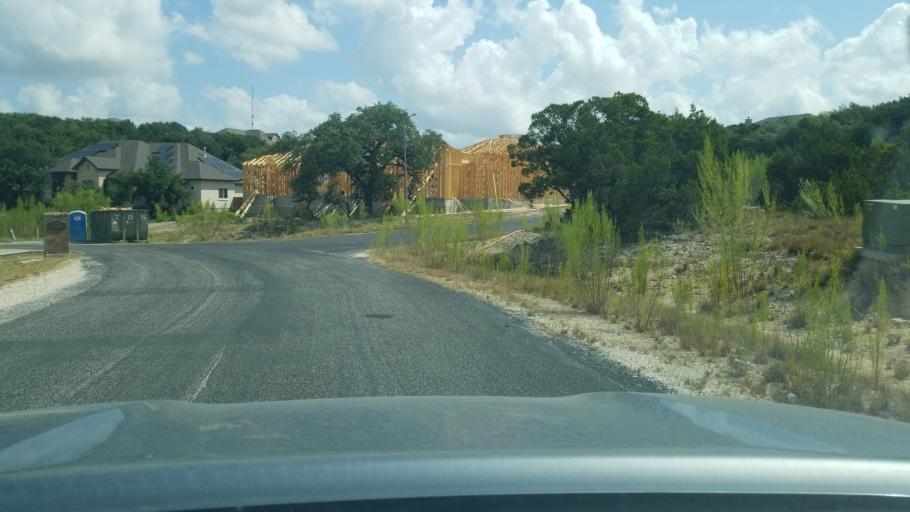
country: US
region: Texas
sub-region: Bexar County
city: Timberwood Park
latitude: 29.6874
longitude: -98.5172
